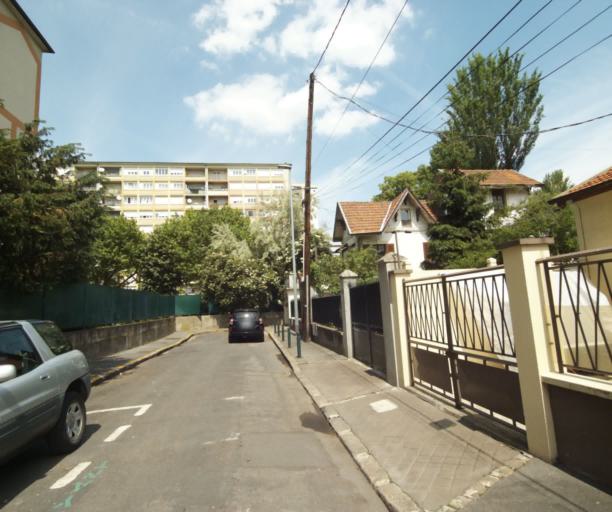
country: FR
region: Ile-de-France
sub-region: Departement des Hauts-de-Seine
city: Colombes
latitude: 48.9267
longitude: 2.2484
